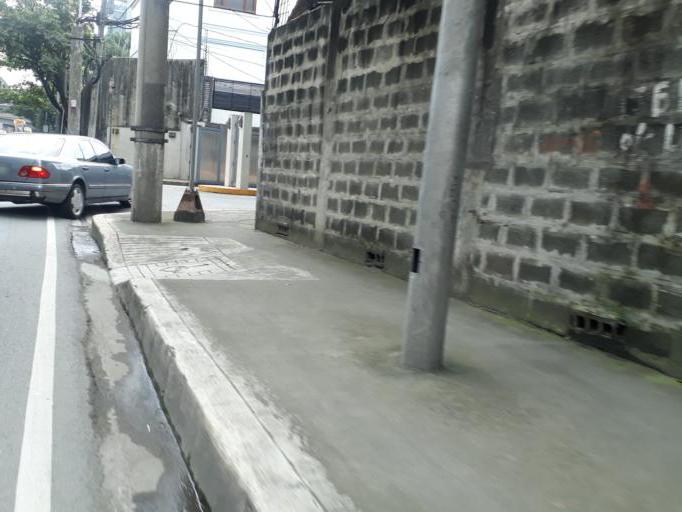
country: PH
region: Metro Manila
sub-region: Pasig
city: Pasig City
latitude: 14.5917
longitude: 121.0797
